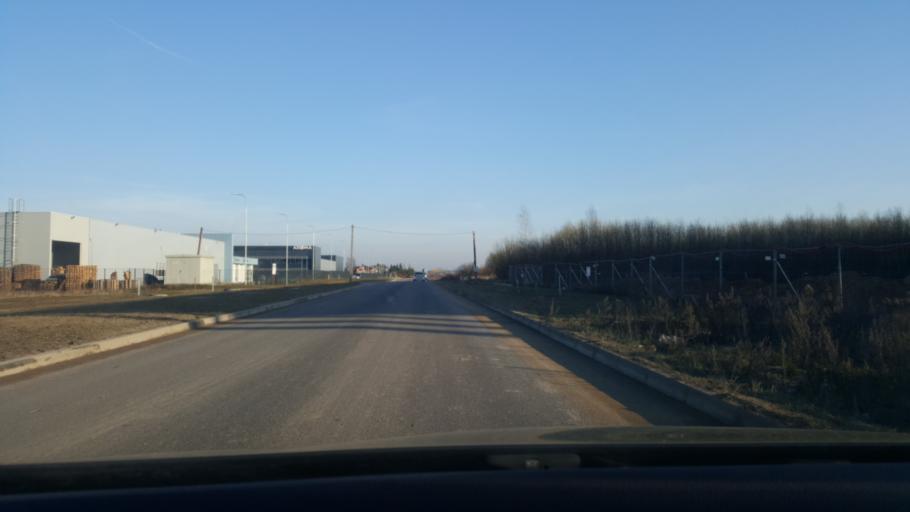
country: LT
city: Ramuciai
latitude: 54.9384
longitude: 24.0144
